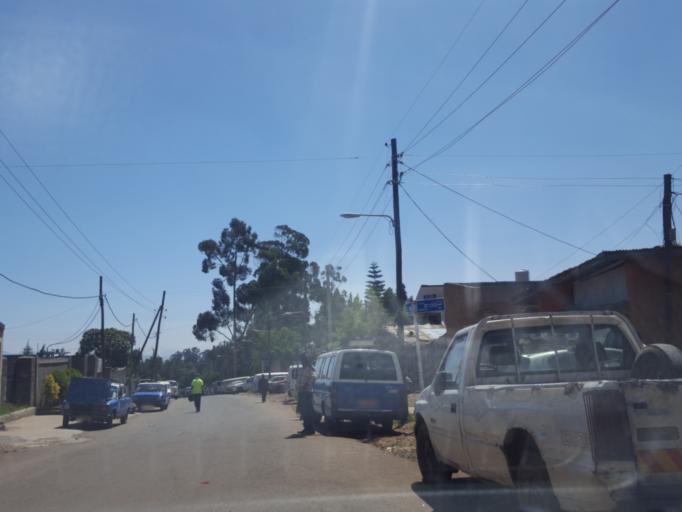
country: ET
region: Adis Abeba
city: Addis Ababa
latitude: 9.0558
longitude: 38.7490
